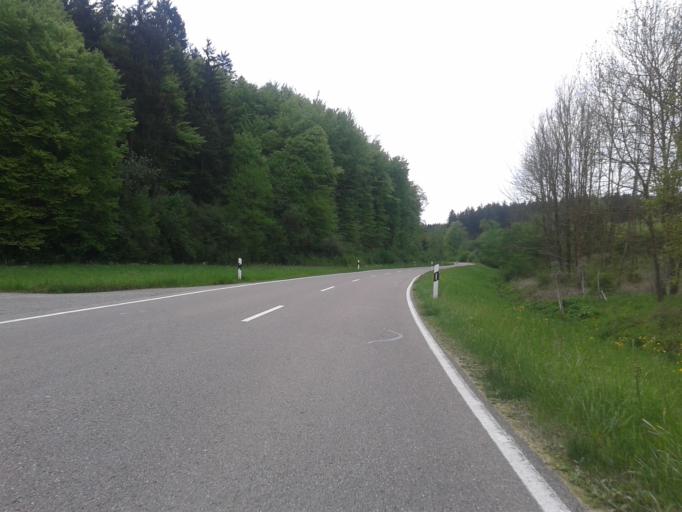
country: DE
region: Baden-Wuerttemberg
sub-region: Tuebingen Region
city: Erbach
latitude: 48.3580
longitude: 9.8447
